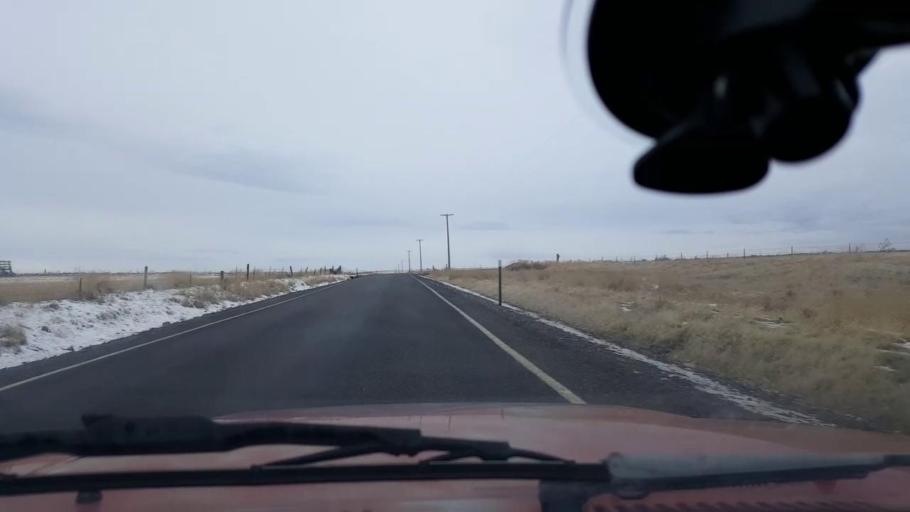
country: US
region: Washington
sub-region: Garfield County
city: Pomeroy
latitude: 46.3221
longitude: -117.3761
